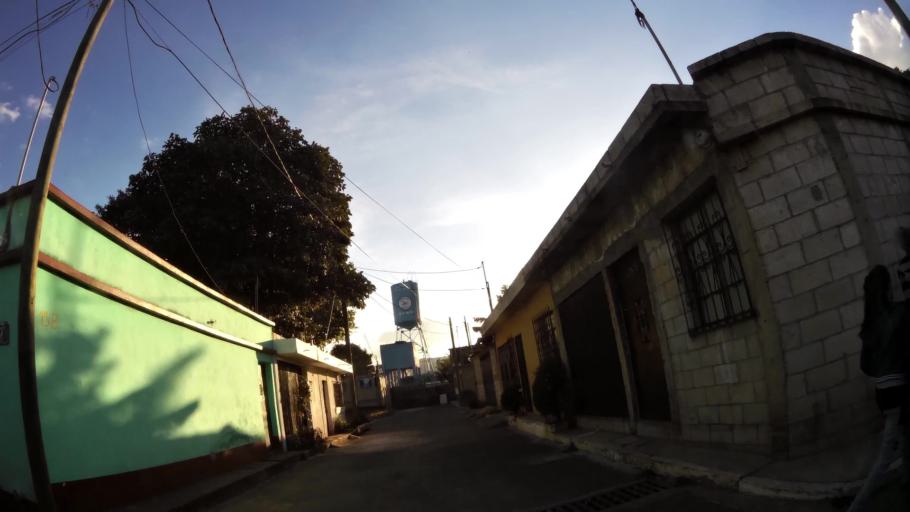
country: GT
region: Guatemala
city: Villa Nueva
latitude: 14.5157
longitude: -90.5832
